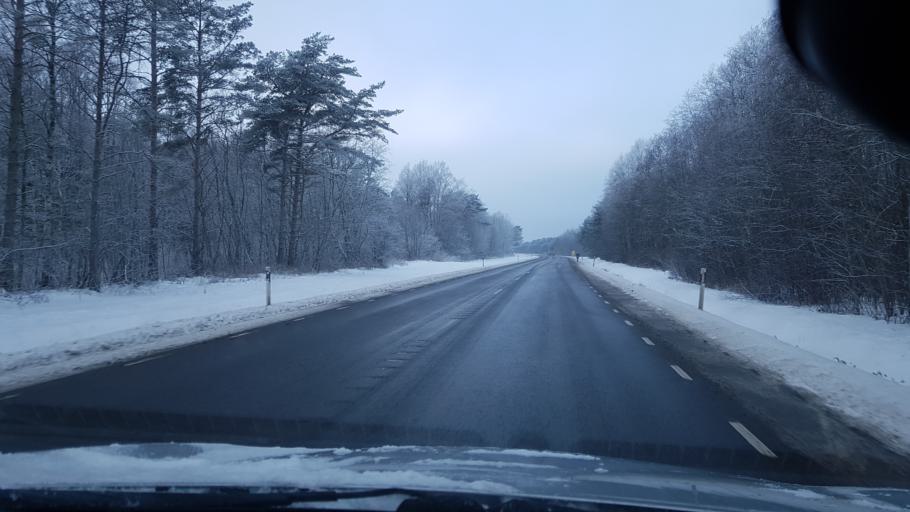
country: EE
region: Harju
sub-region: Paldiski linn
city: Paldiski
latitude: 59.3382
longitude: 24.2222
